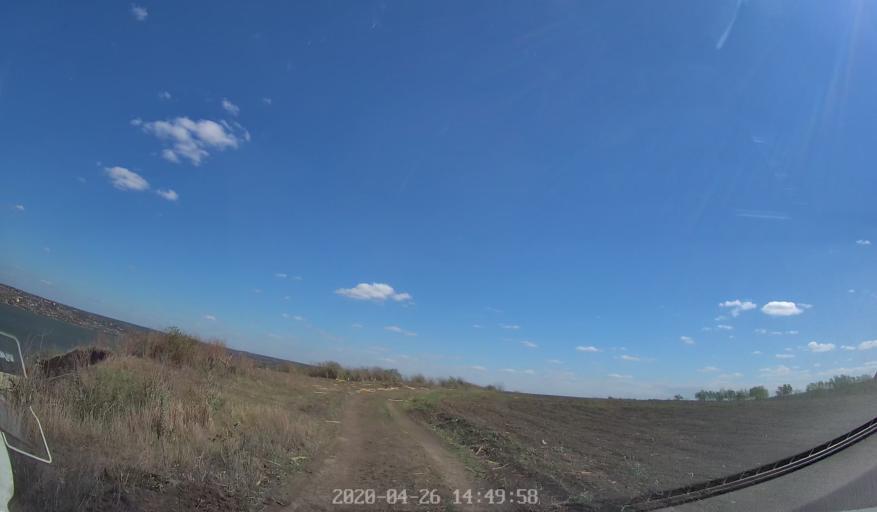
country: MD
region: Telenesti
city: Cocieri
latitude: 47.3587
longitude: 29.0646
